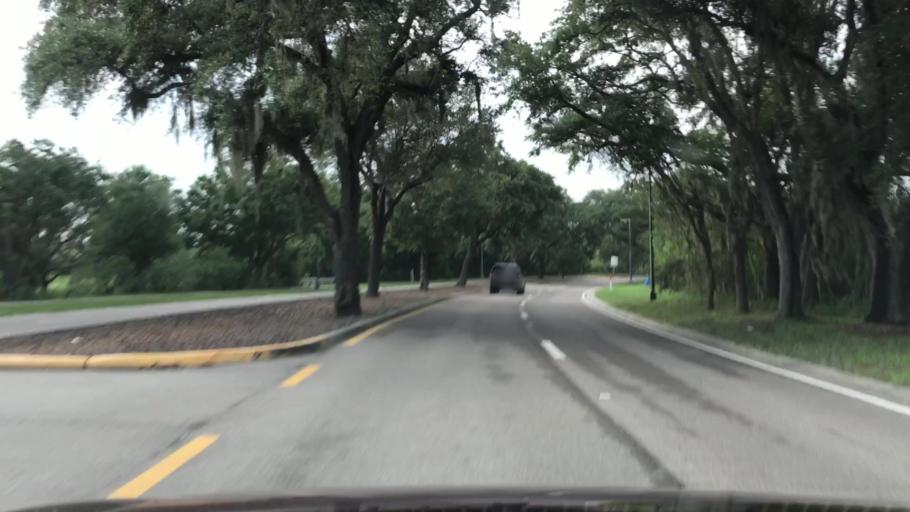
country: US
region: Florida
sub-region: Sarasota County
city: Venice Gardens
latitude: 27.0594
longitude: -82.3955
